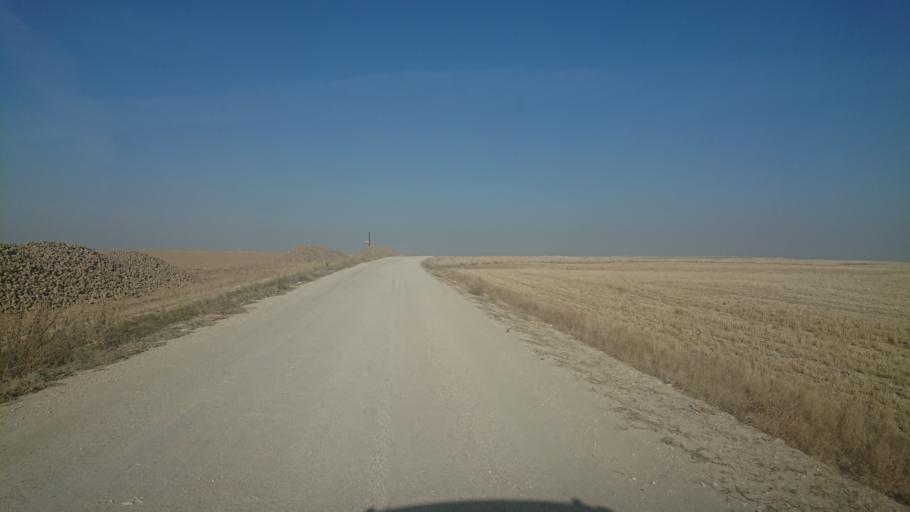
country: TR
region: Aksaray
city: Sultanhani
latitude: 38.0514
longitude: 33.6111
